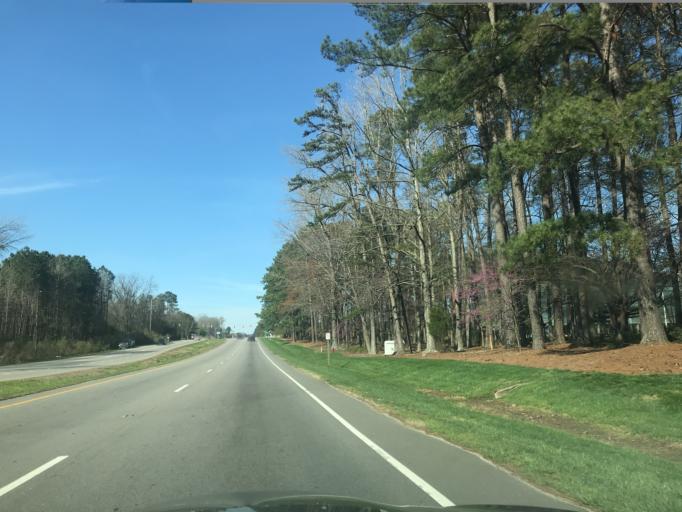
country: US
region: North Carolina
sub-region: Wake County
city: Garner
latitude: 35.6517
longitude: -78.7068
